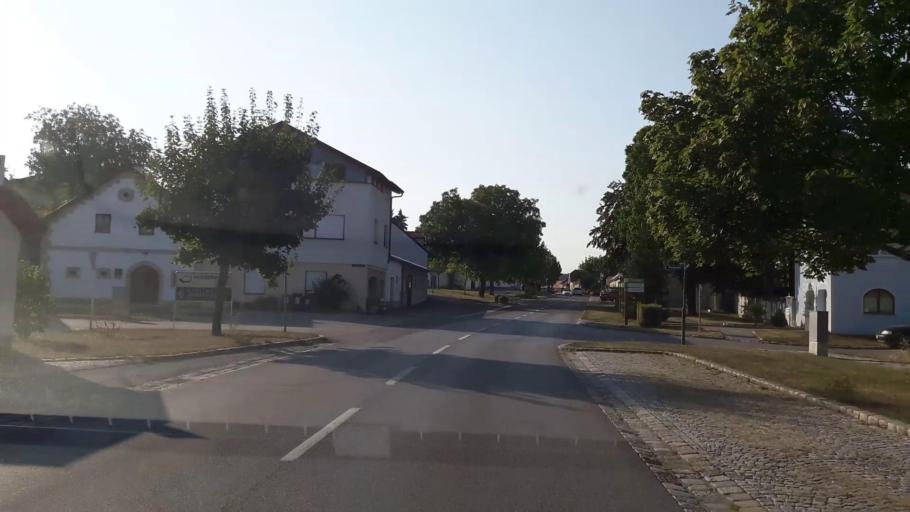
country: AT
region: Lower Austria
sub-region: Politischer Bezirk Ganserndorf
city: Orth an der Donau
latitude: 48.0672
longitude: 16.7052
